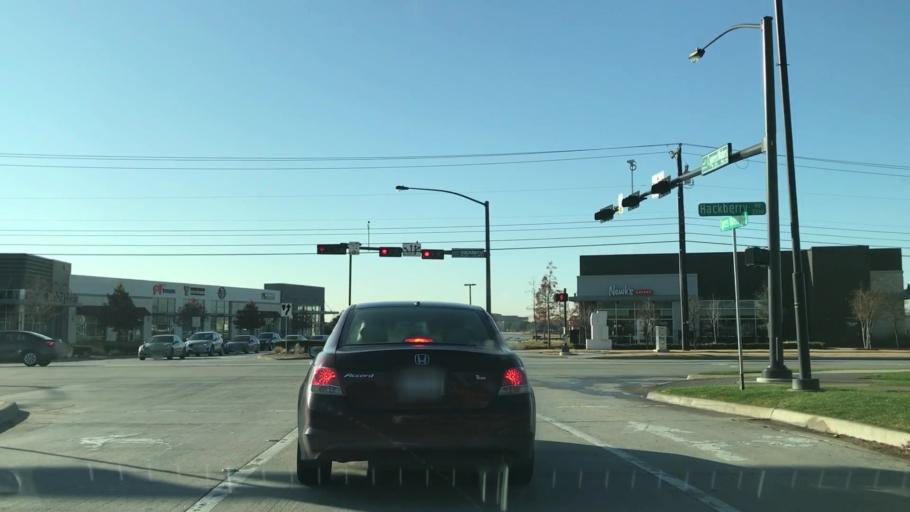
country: US
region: Texas
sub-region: Dallas County
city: Coppell
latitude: 32.9260
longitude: -96.9906
